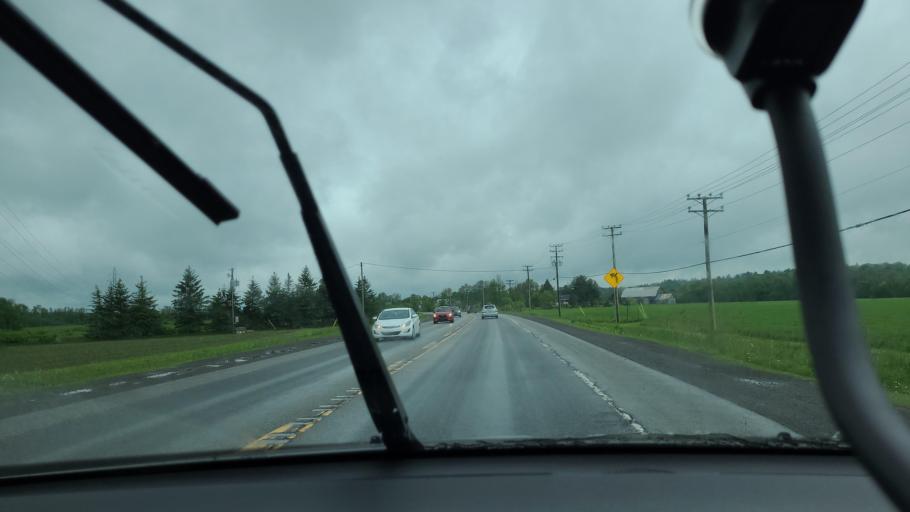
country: CA
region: Quebec
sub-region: Laurentides
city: Saint-Jerome
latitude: 45.7458
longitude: -74.0185
